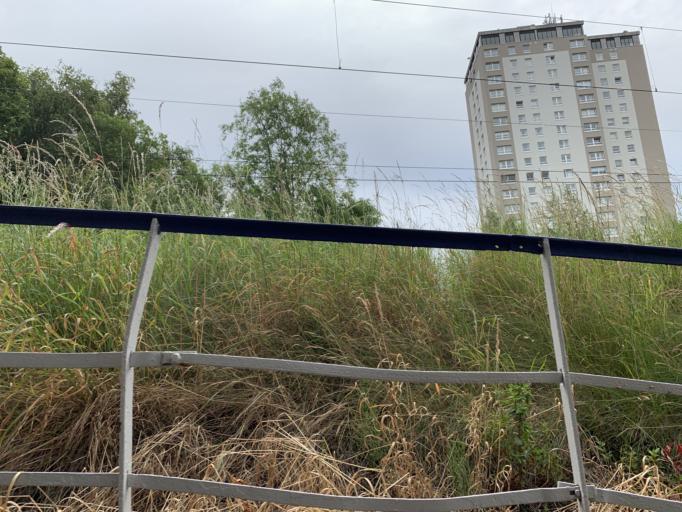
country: GB
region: Scotland
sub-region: East Renfrewshire
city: Giffnock
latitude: 55.8250
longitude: -4.2609
